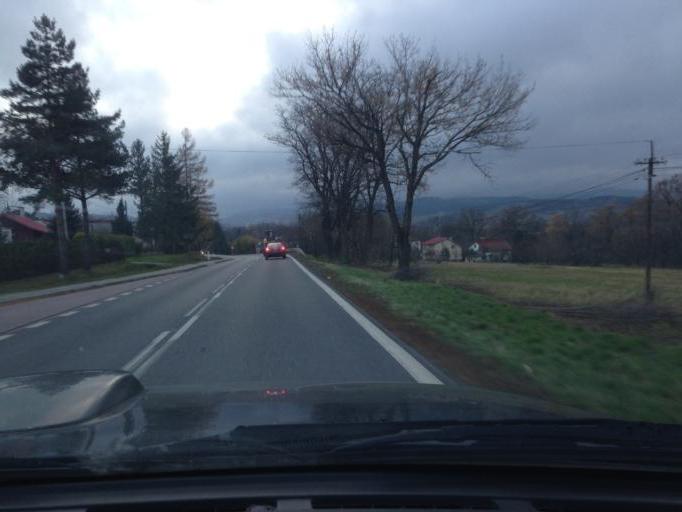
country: PL
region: Subcarpathian Voivodeship
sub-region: Powiat jasielski
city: Nowy Zmigrod
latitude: 49.6152
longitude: 21.5346
